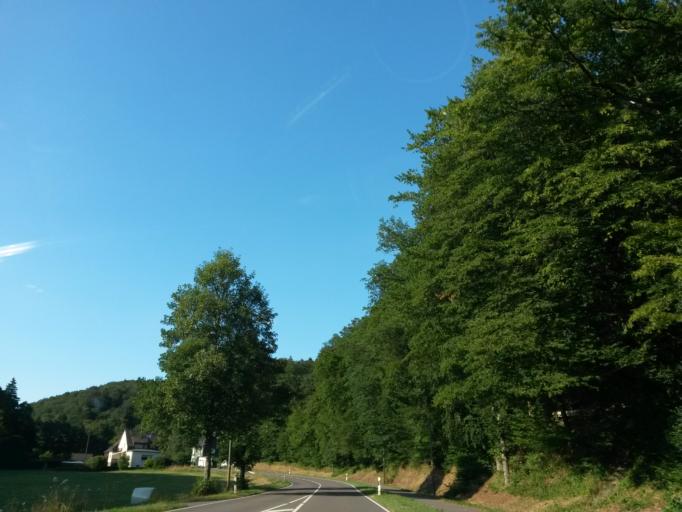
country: DE
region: North Rhine-Westphalia
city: Bergneustadt
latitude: 51.0608
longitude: 7.6543
